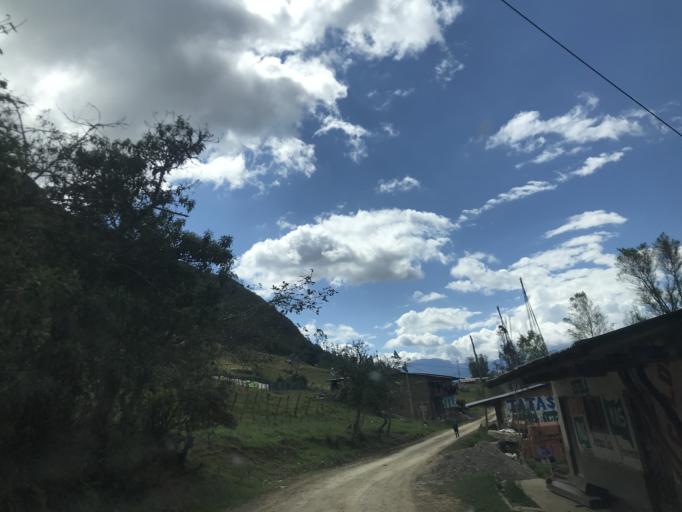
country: PE
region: Cajamarca
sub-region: Provincia de Chota
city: Querocoto
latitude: -6.3360
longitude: -79.0674
